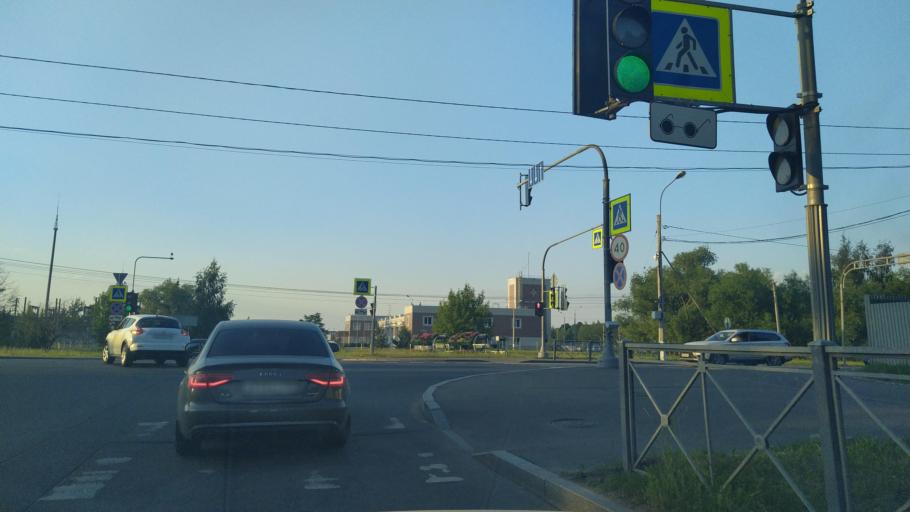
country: RU
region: St.-Petersburg
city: Kronshtadt
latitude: 60.0106
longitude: 29.7277
